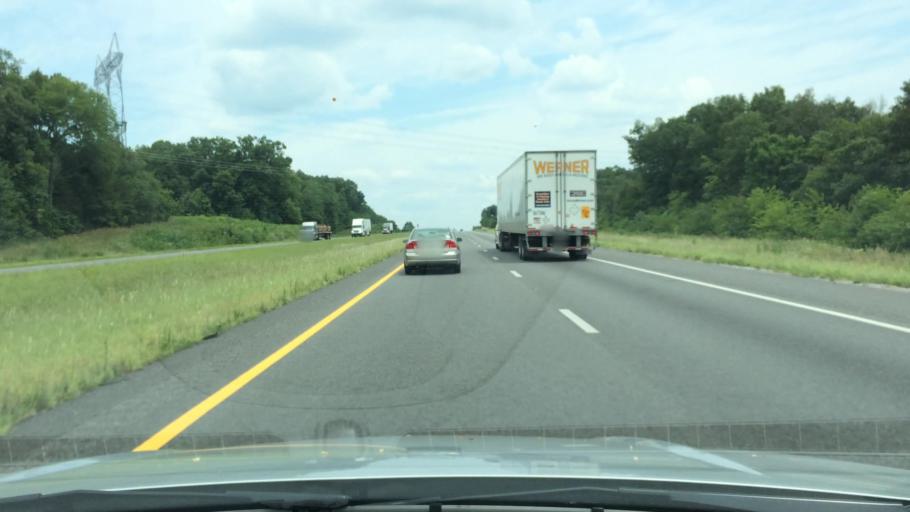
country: US
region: Tennessee
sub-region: Maury County
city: Spring Hill
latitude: 35.7074
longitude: -86.8809
